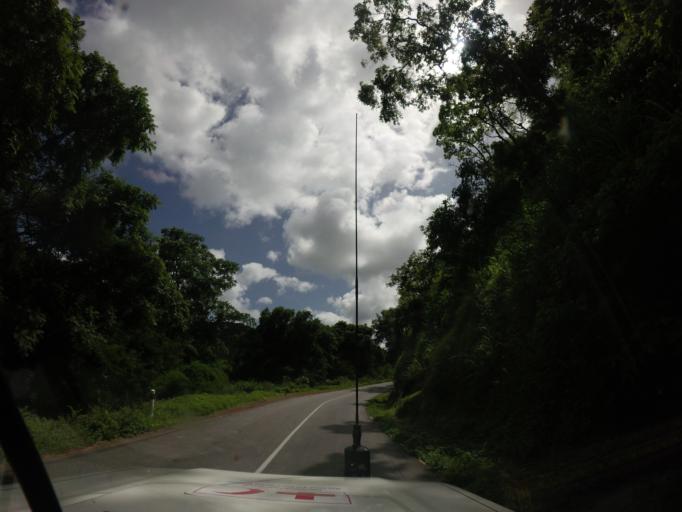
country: GN
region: Mamou
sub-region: Mamou Prefecture
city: Mamou
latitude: 10.2933
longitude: -11.9462
